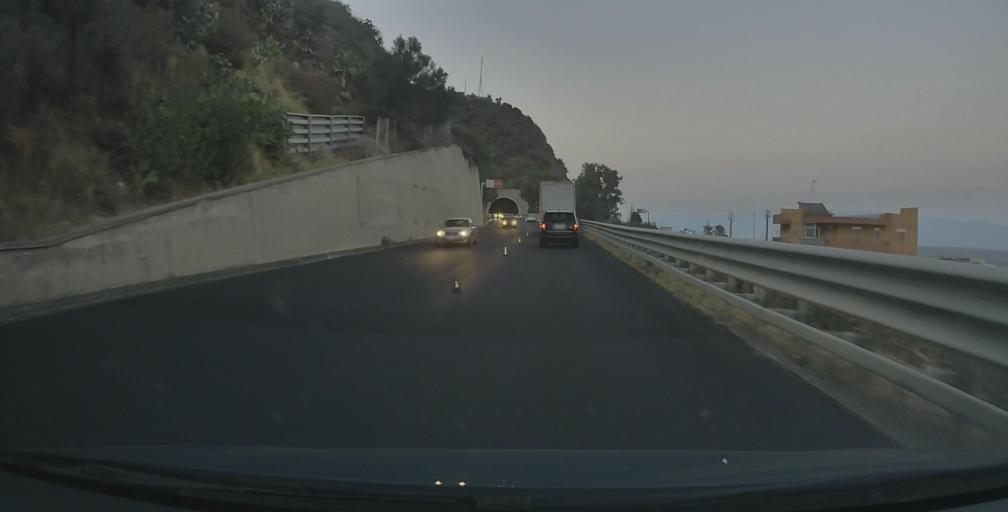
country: IT
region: Sicily
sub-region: Messina
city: Guidomandri Marina
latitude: 38.0449
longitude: 15.4612
